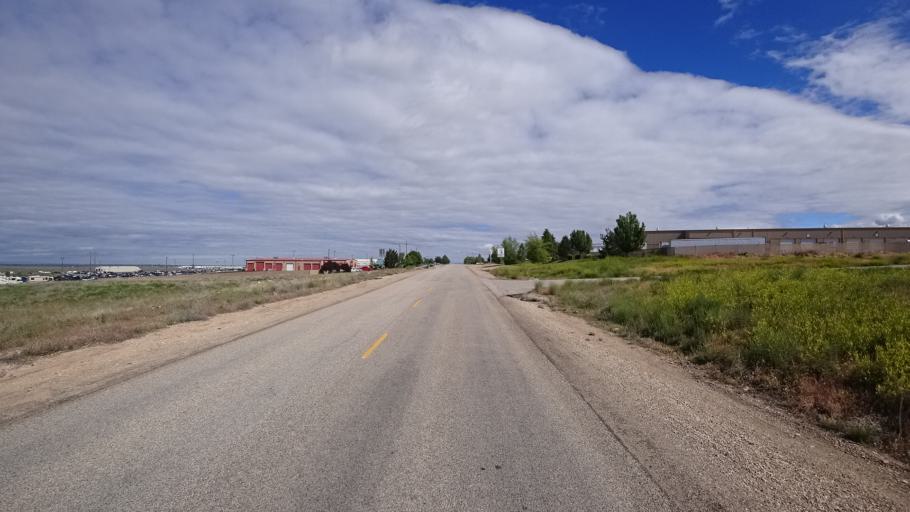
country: US
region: Idaho
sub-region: Ada County
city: Boise
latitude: 43.5329
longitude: -116.1591
